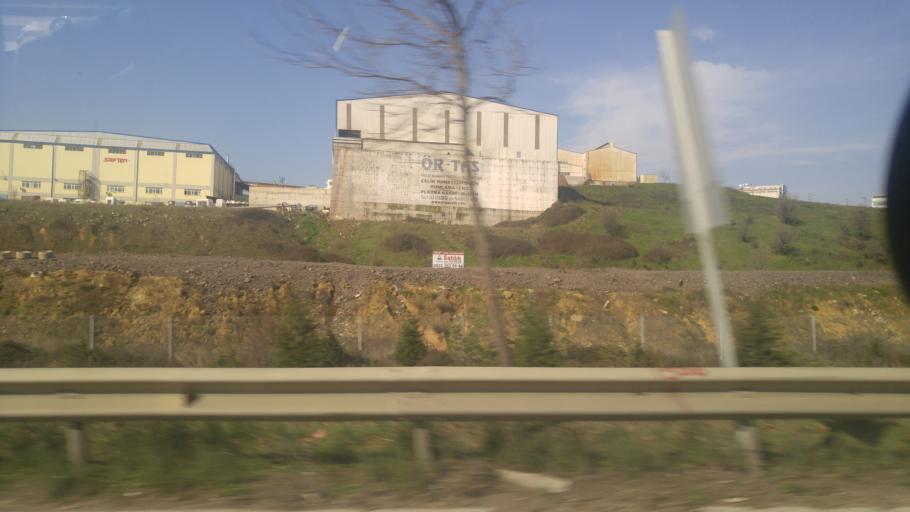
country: TR
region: Kocaeli
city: Balcik
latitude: 40.8436
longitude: 29.3741
